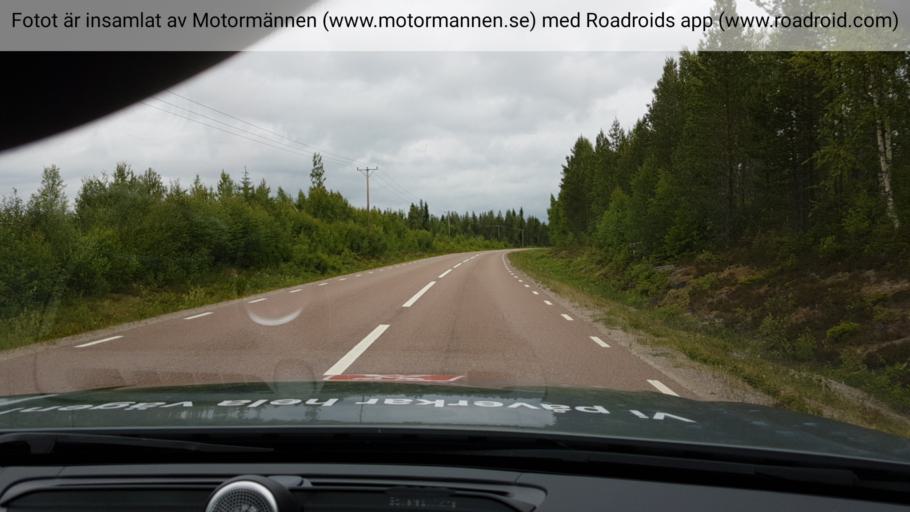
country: SE
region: Jaemtland
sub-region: Braecke Kommun
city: Braecke
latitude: 62.9279
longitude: 15.6812
